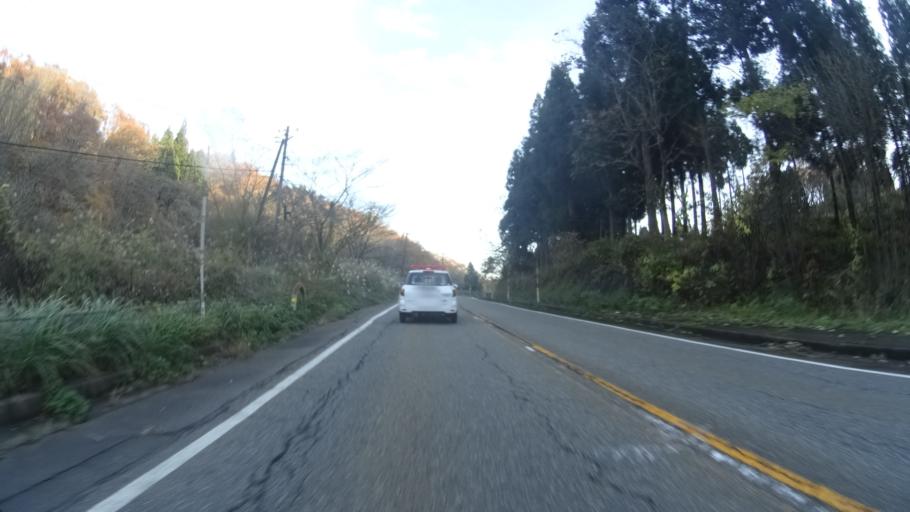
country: JP
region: Niigata
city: Kashiwazaki
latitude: 37.4123
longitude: 138.6838
